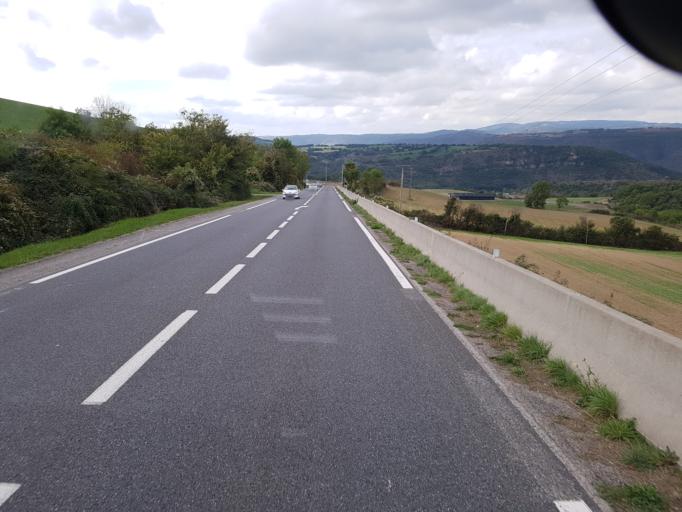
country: FR
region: Midi-Pyrenees
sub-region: Departement de l'Aveyron
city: Saint-Georges-de-Luzencon
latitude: 44.0799
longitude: 3.0027
